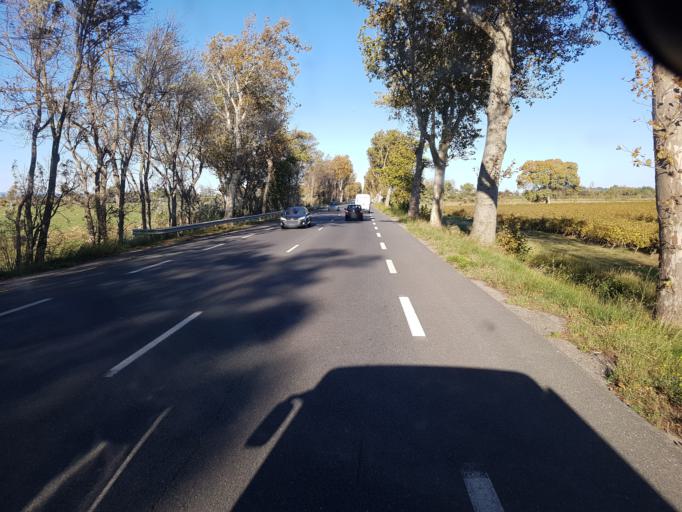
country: FR
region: Languedoc-Roussillon
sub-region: Departement de l'Aude
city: Coursan
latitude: 43.2158
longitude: 3.0347
